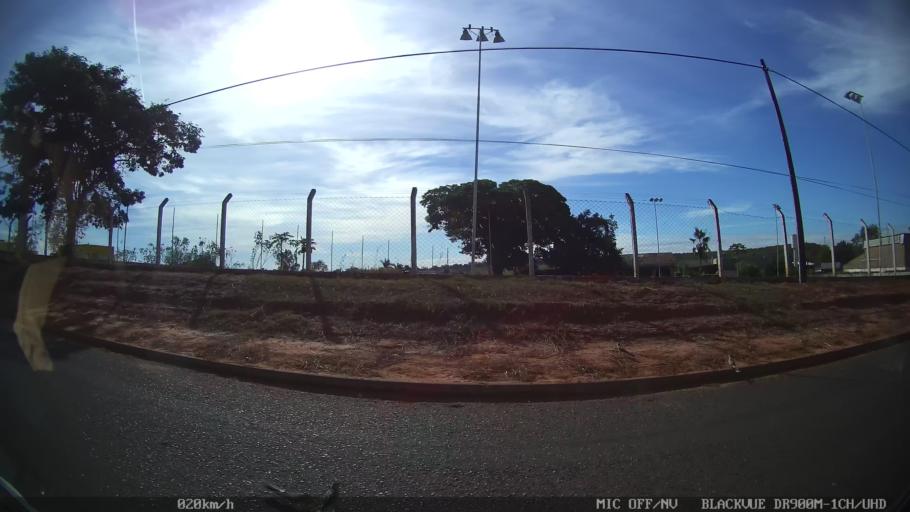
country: BR
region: Sao Paulo
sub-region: Sao Jose Do Rio Preto
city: Sao Jose do Rio Preto
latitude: -20.7970
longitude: -49.3246
